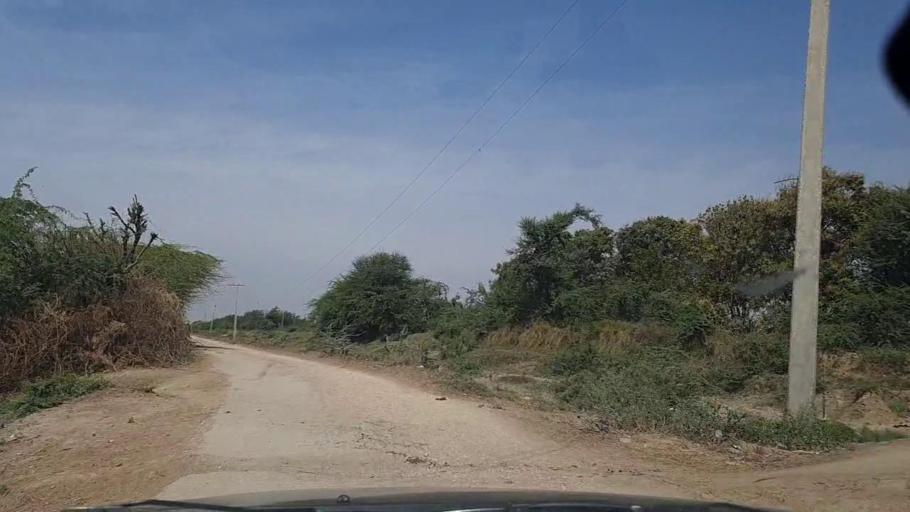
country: PK
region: Sindh
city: Mirpur Batoro
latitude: 24.6461
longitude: 68.1900
